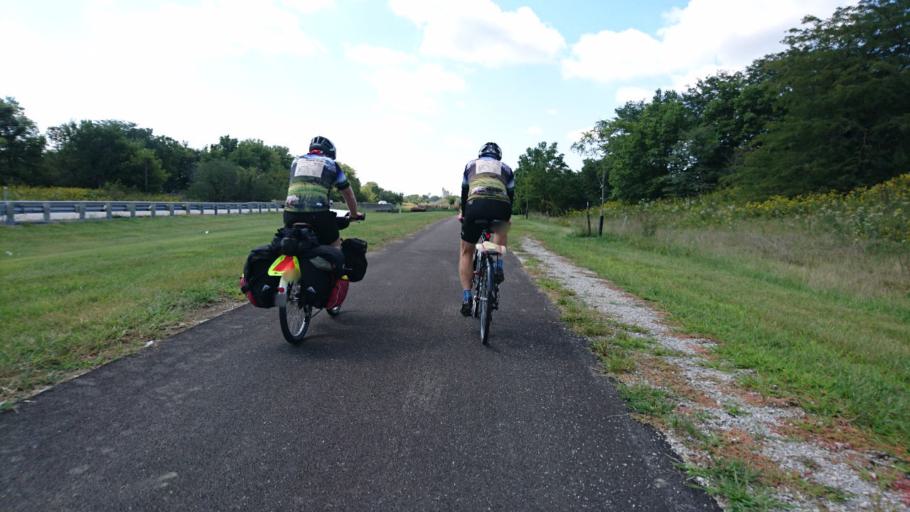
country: US
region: Illinois
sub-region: McLean County
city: Hudson
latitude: 40.5736
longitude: -88.8843
